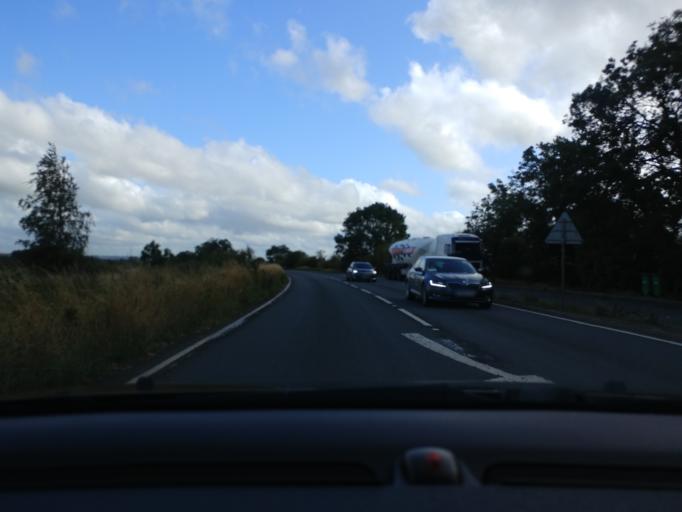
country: GB
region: England
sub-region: Oxfordshire
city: Bicester
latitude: 51.8777
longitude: -1.2305
